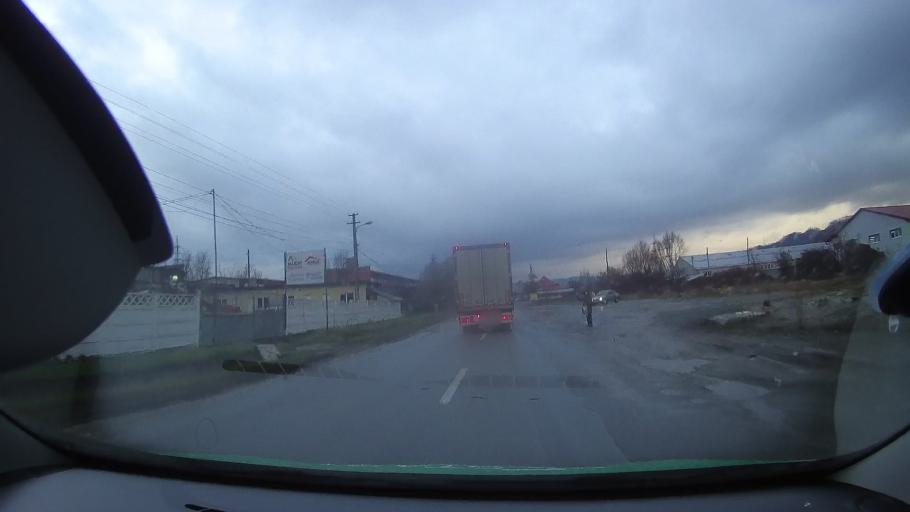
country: RO
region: Hunedoara
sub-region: Municipiul Brad
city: Brad
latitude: 46.1425
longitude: 22.7758
